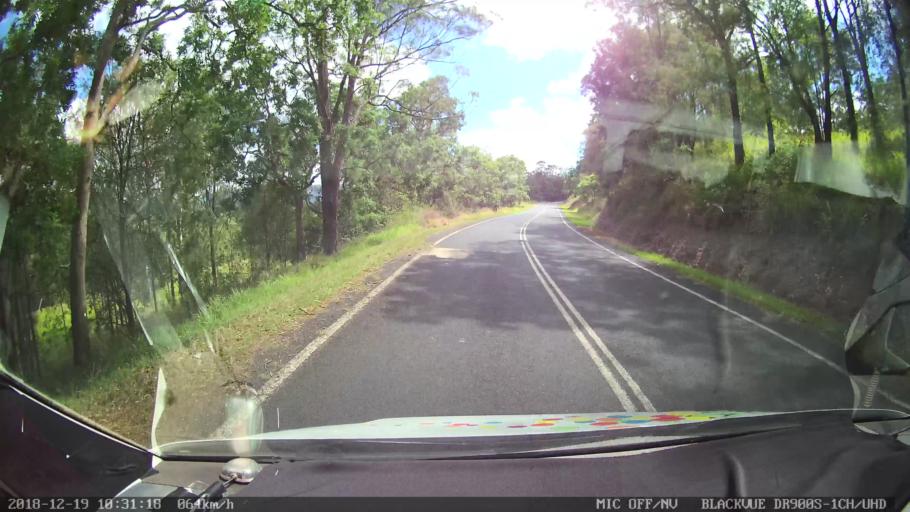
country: AU
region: New South Wales
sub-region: Lismore Municipality
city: Larnook
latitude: -28.5904
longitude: 153.1153
